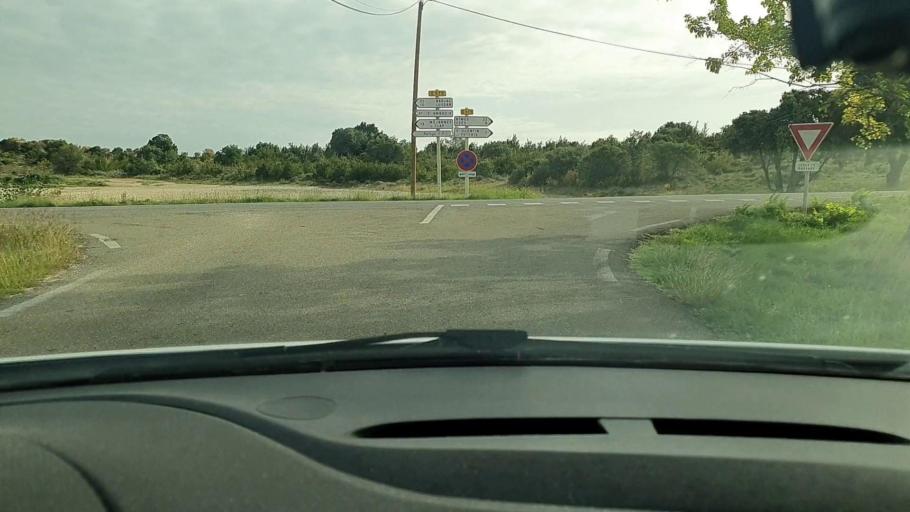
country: FR
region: Languedoc-Roussillon
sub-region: Departement du Gard
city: Montaren-et-Saint-Mediers
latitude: 44.0849
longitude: 4.3905
